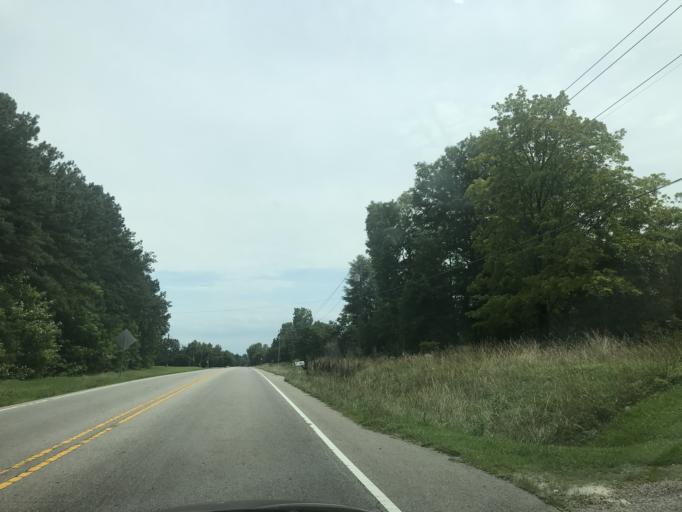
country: US
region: North Carolina
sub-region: Vance County
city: South Henderson
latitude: 36.2916
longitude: -78.4053
